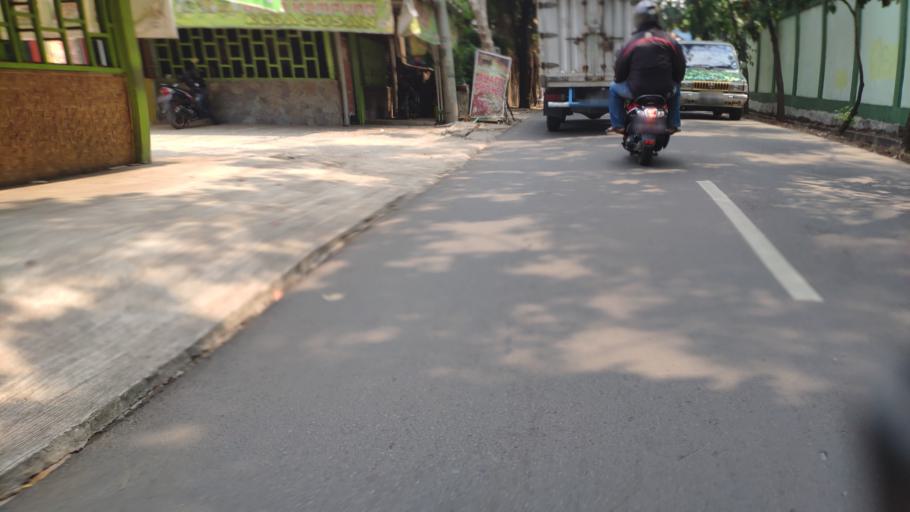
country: ID
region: West Java
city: Depok
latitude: -6.3115
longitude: 106.8258
